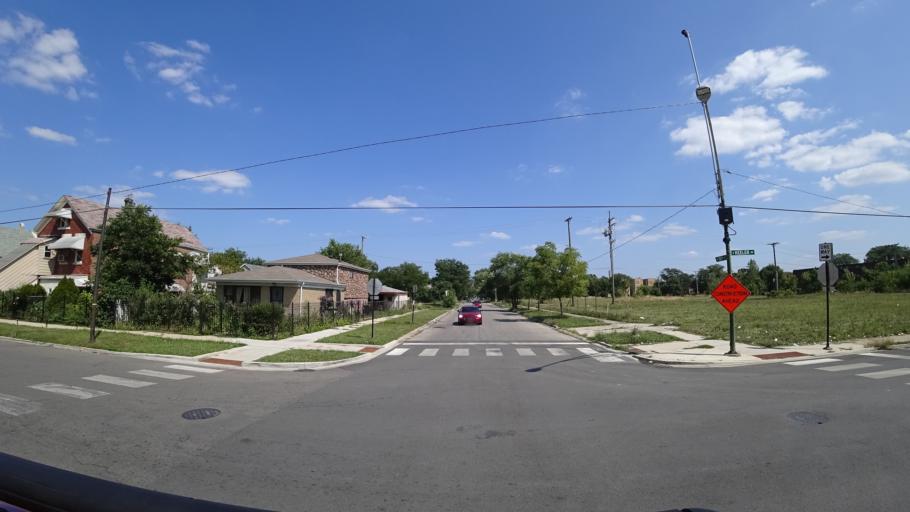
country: US
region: Illinois
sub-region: Cook County
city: Cicero
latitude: 41.8570
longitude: -87.7298
